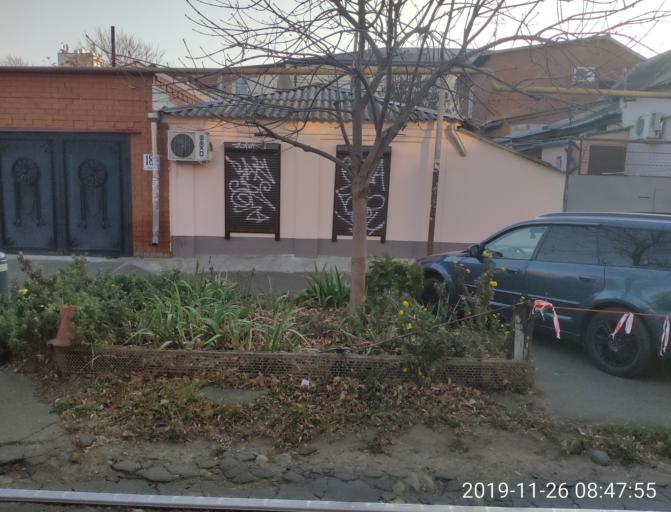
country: RU
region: Krasnodarskiy
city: Krasnodar
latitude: 45.0366
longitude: 38.9789
